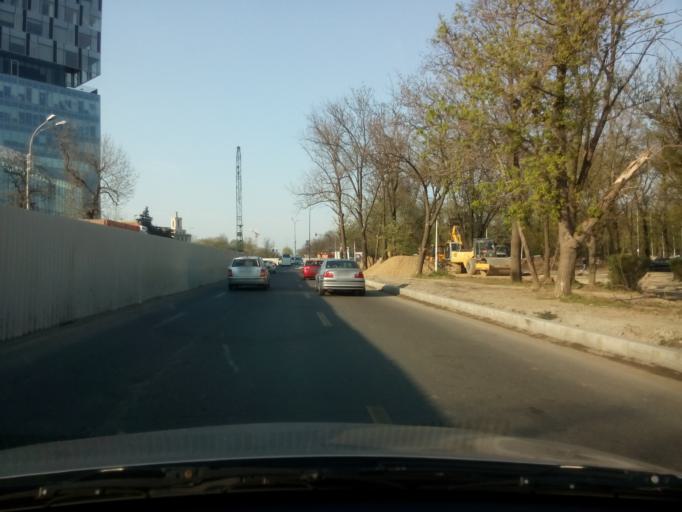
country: RO
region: Bucuresti
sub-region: Municipiul Bucuresti
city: Bucuresti
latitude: 44.4765
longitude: 26.0715
